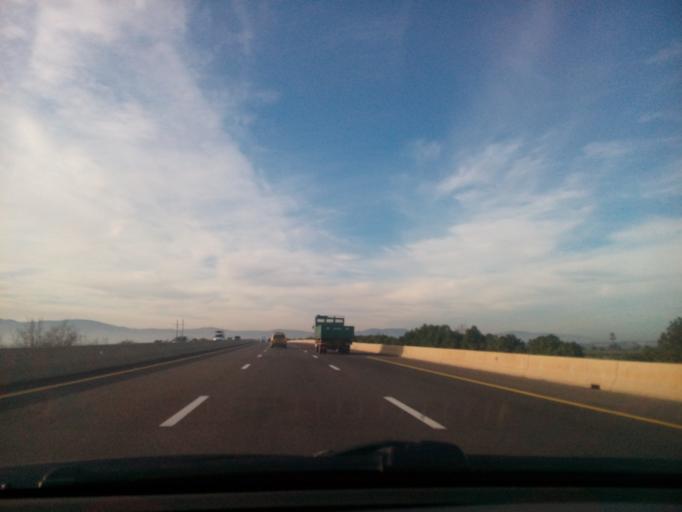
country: DZ
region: Mascara
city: Sig
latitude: 35.6008
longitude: -0.0385
